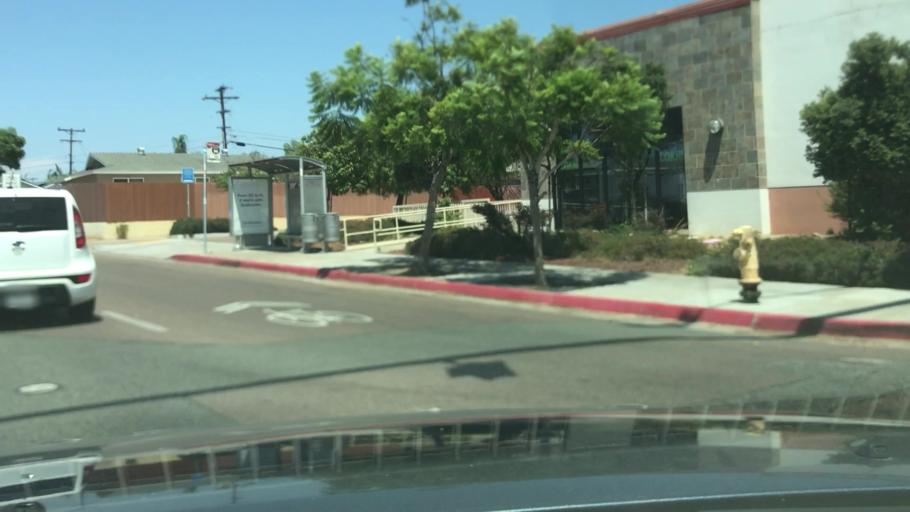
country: US
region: California
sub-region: San Diego County
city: La Jolla
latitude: 32.8346
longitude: -117.1948
